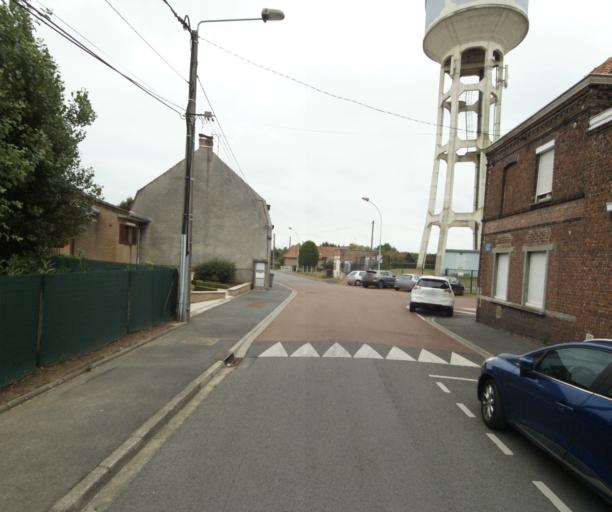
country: FR
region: Nord-Pas-de-Calais
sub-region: Departement du Nord
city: Leers
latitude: 50.6789
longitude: 3.2345
